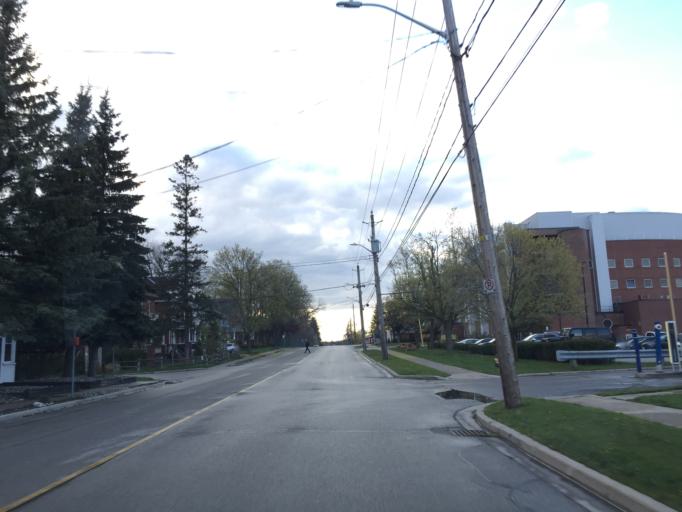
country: CA
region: Ontario
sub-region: Wellington County
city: Guelph
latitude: 43.5549
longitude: -80.2525
